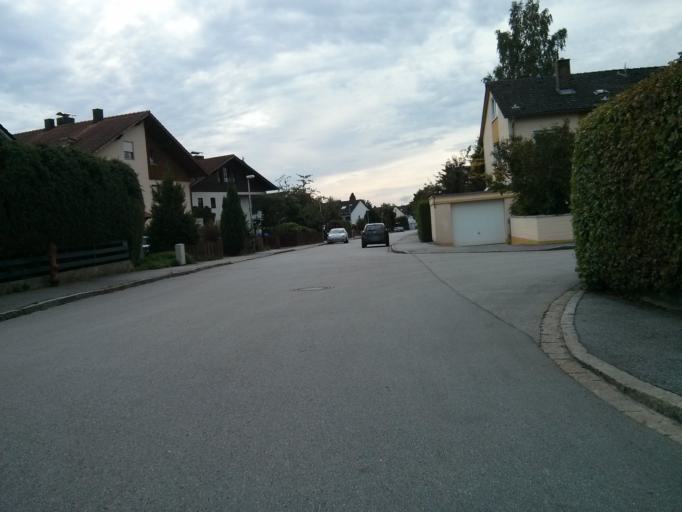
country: DE
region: Bavaria
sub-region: Lower Bavaria
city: Deggendorf
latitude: 48.8490
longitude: 12.9719
